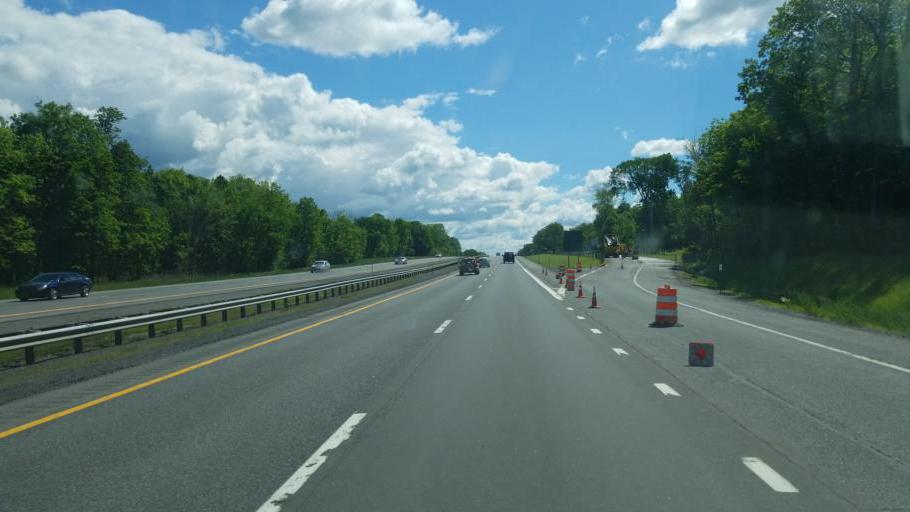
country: US
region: New York
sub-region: Oneida County
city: Vernon
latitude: 43.1297
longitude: -75.5349
